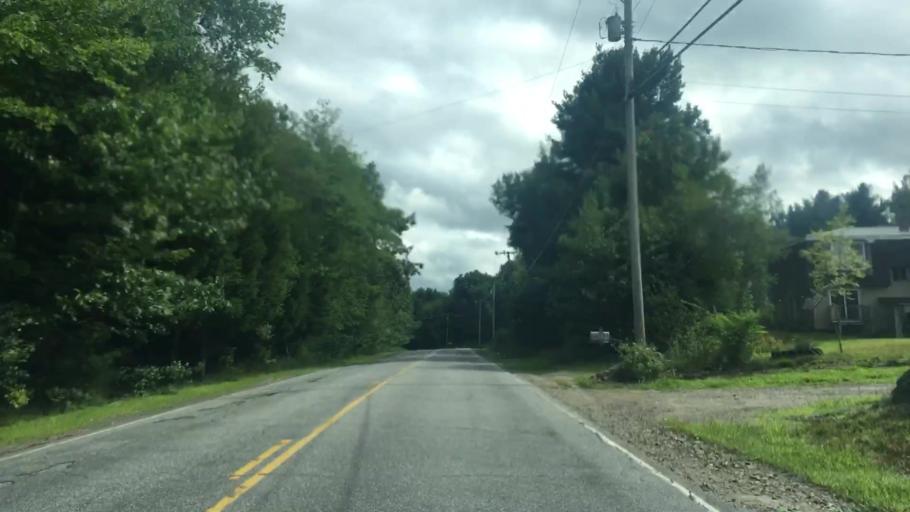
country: US
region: Maine
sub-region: York County
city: Waterboro
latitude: 43.5669
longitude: -70.7033
